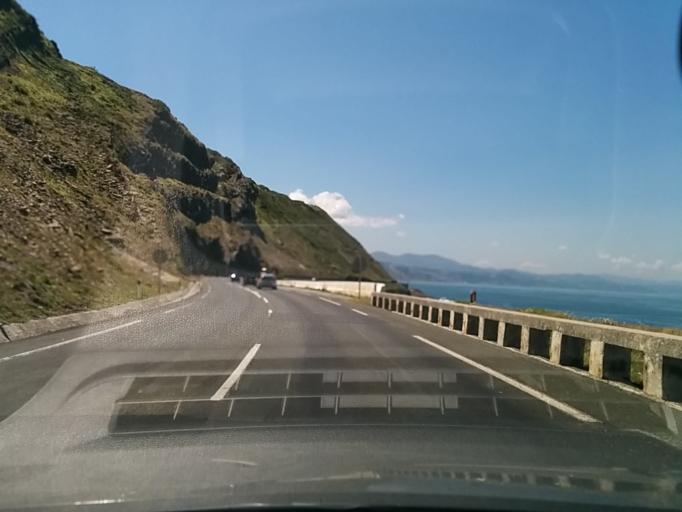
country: ES
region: Basque Country
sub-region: Provincia de Guipuzcoa
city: Getaria
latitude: 43.3098
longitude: -2.2305
